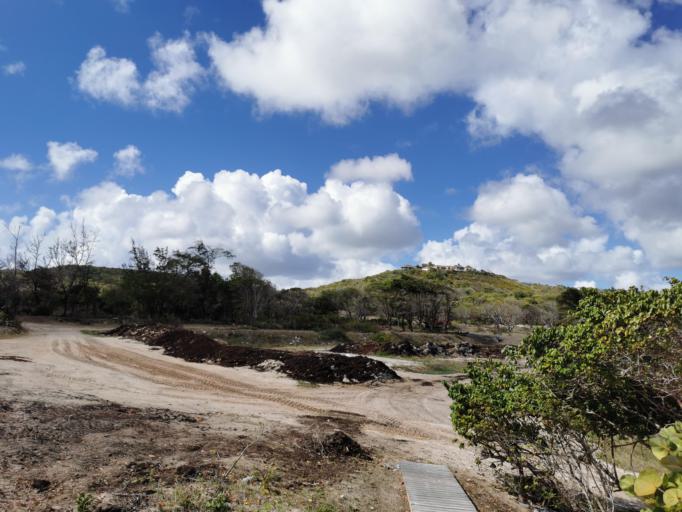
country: AG
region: Saint Paul
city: Falmouth
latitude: 17.0352
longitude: -61.6889
